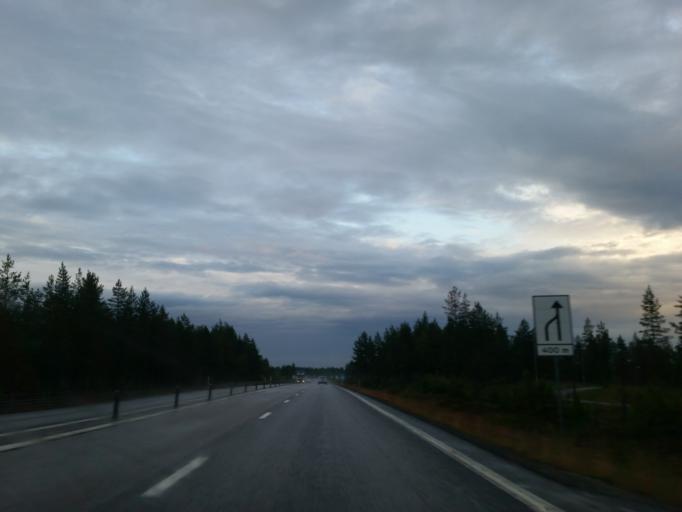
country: SE
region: Vaesterbotten
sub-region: Umea Kommun
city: Saevar
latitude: 63.8875
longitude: 20.5098
